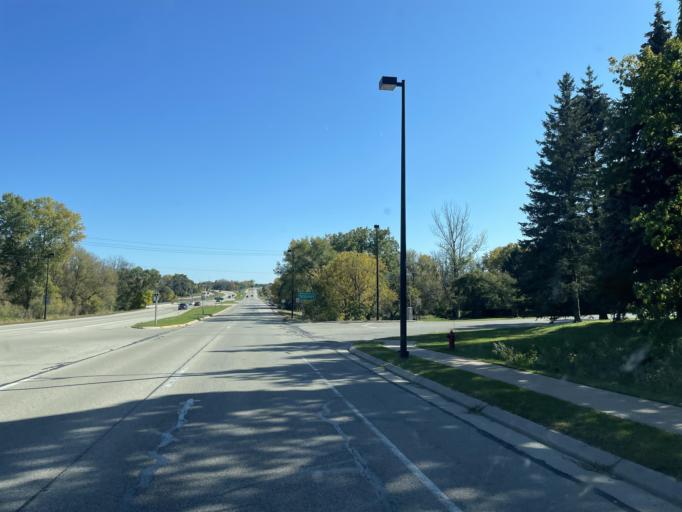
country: US
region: Wisconsin
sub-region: Waukesha County
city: Butler
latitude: 43.1418
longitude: -88.0654
